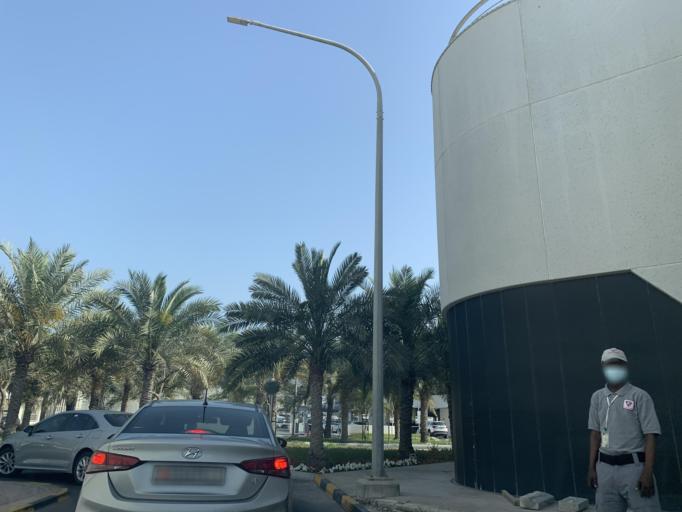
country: BH
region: Muharraq
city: Al Muharraq
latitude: 26.2619
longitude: 50.5987
